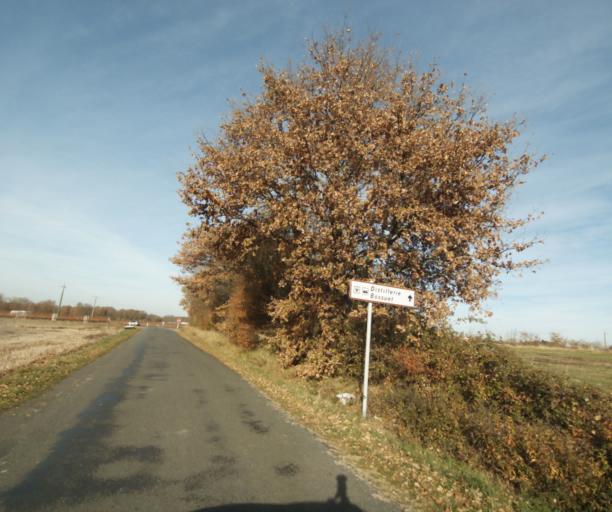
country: FR
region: Poitou-Charentes
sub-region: Departement de la Charente-Maritime
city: Chaniers
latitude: 45.7283
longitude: -0.5272
